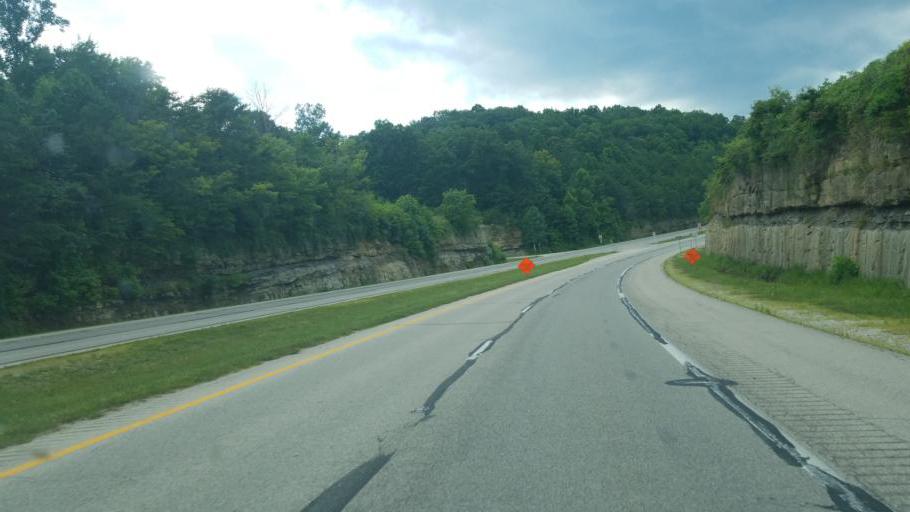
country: US
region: West Virginia
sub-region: Kanawha County
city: Alum Creek
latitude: 38.2666
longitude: -81.7916
